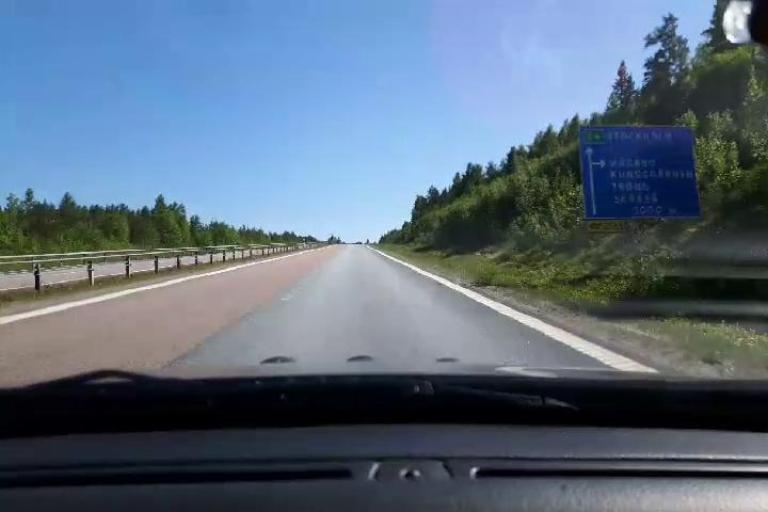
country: SE
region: Gaevleborg
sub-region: Soderhamns Kommun
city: Soderhamn
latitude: 61.3509
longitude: 17.0175
